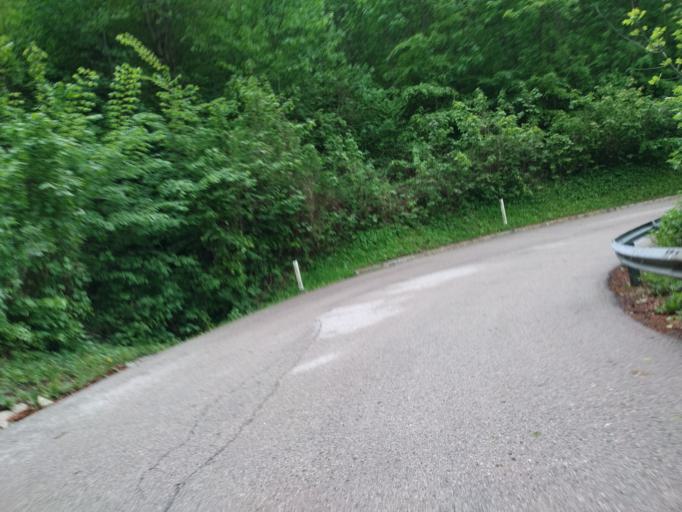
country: AT
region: Lower Austria
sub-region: Politischer Bezirk Wien-Umgebung
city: Mauerbach
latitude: 48.2426
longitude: 16.2208
